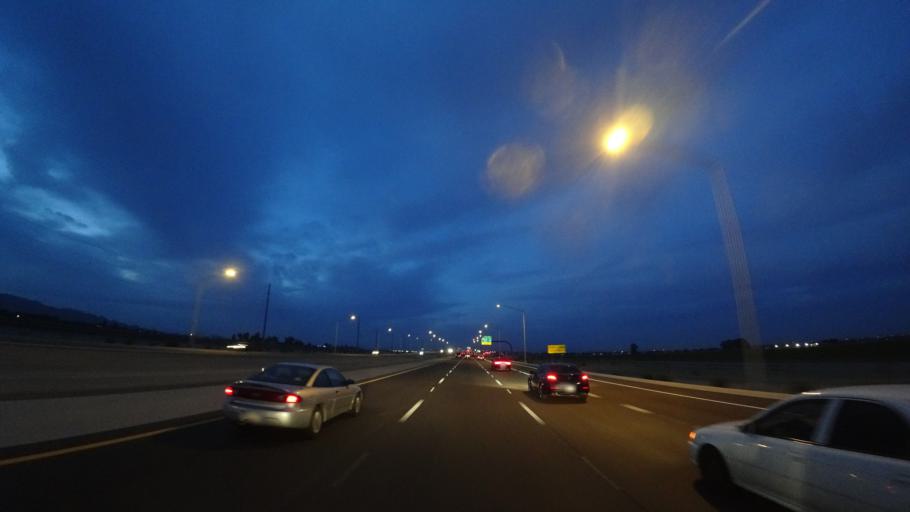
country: US
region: Arizona
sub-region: Maricopa County
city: Citrus Park
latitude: 33.5732
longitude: -112.4180
